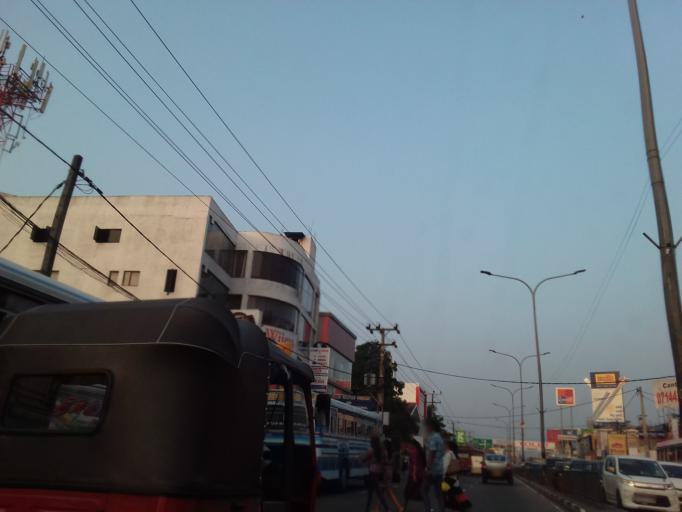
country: LK
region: Western
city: Kelaniya
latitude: 6.9810
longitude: 79.9299
